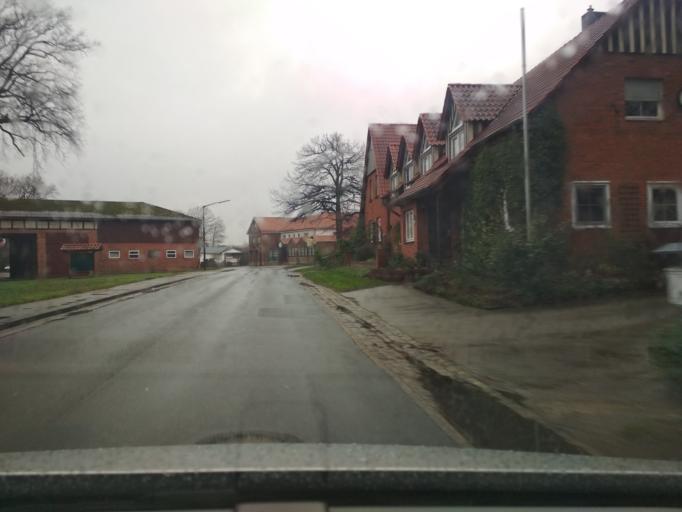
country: DE
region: Lower Saxony
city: Hankensbuttel
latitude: 52.7139
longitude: 10.6249
